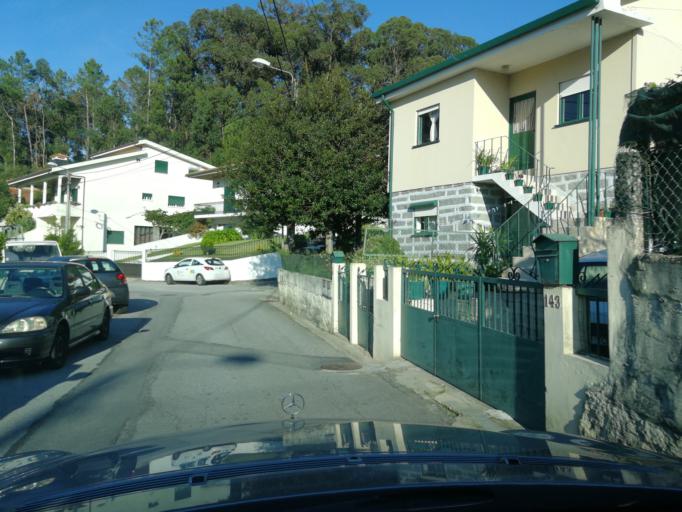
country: PT
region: Braga
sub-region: Vila Nova de Famalicao
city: Vila Nova de Famalicao
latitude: 41.4270
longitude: -8.5184
